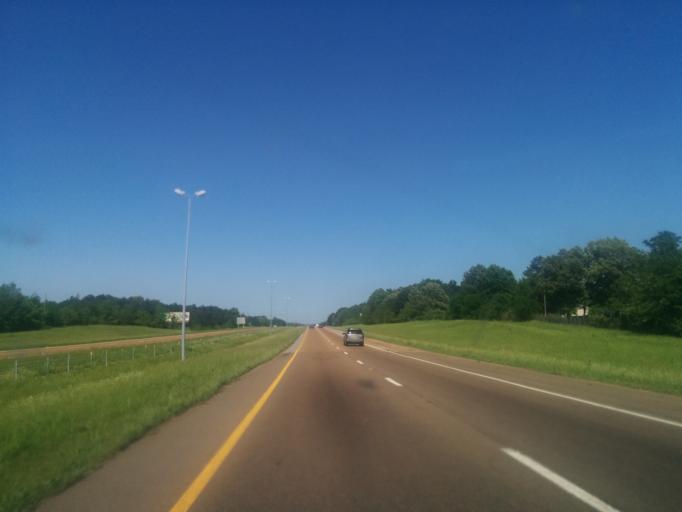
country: US
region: Mississippi
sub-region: Hinds County
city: Jackson
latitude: 32.3715
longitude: -90.2182
